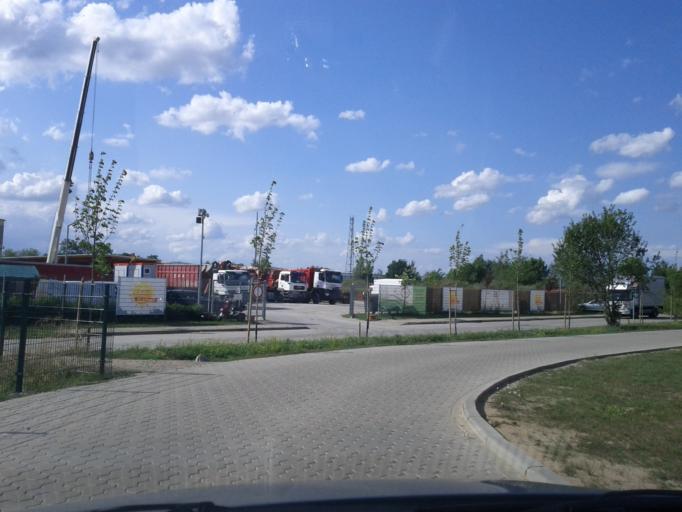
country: DE
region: Brandenburg
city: Hoppegarten
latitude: 52.5096
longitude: 13.6472
